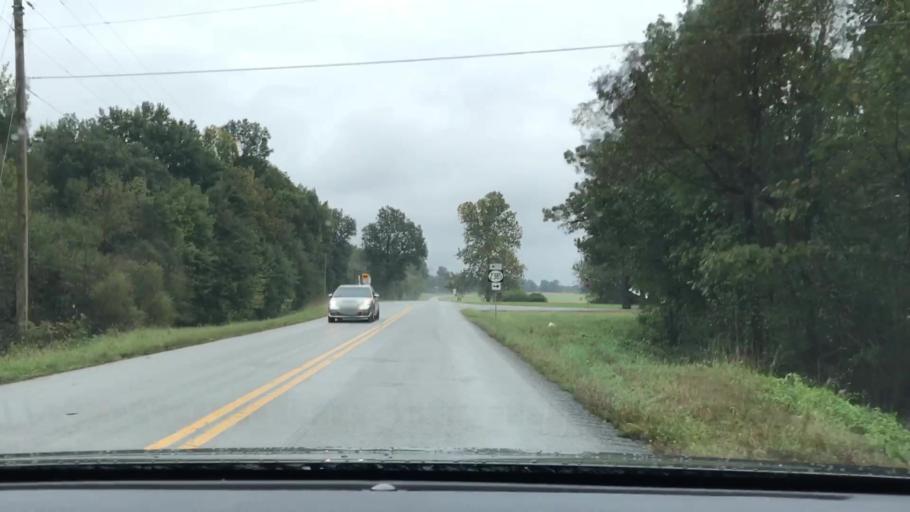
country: US
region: Kentucky
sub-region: McLean County
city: Calhoun
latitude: 37.4739
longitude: -87.2416
